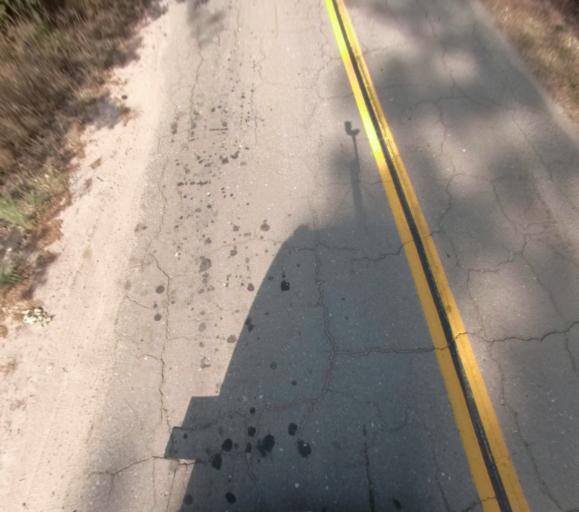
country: US
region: California
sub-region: Madera County
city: Oakhurst
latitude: 37.2603
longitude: -119.5341
